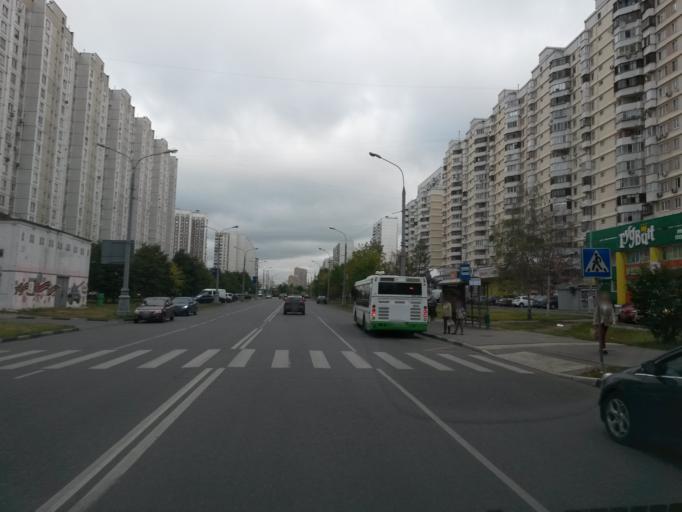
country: RU
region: Moscow
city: Brateyevo
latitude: 55.6533
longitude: 37.7658
